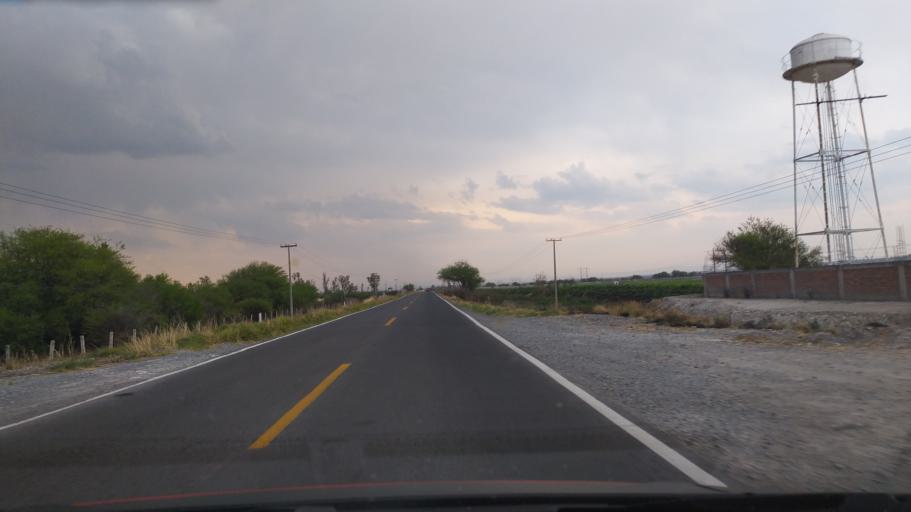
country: MX
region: Guanajuato
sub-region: San Francisco del Rincon
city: San Ignacio de Hidalgo
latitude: 20.8440
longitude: -101.8967
